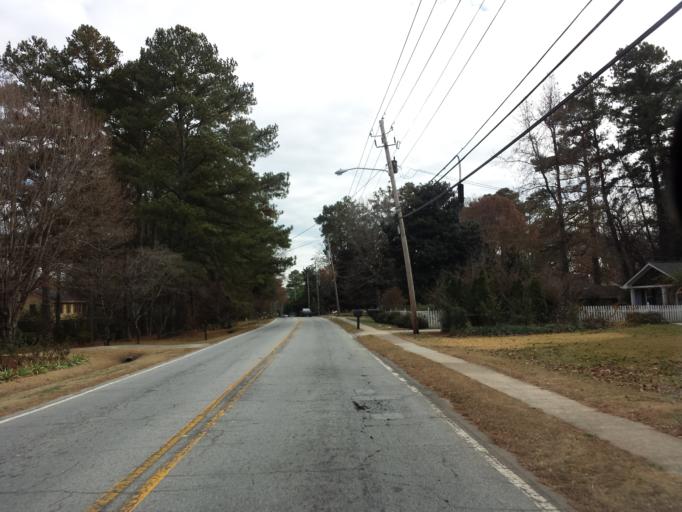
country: US
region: Georgia
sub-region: DeKalb County
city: Dunwoody
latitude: 33.9410
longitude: -84.3297
